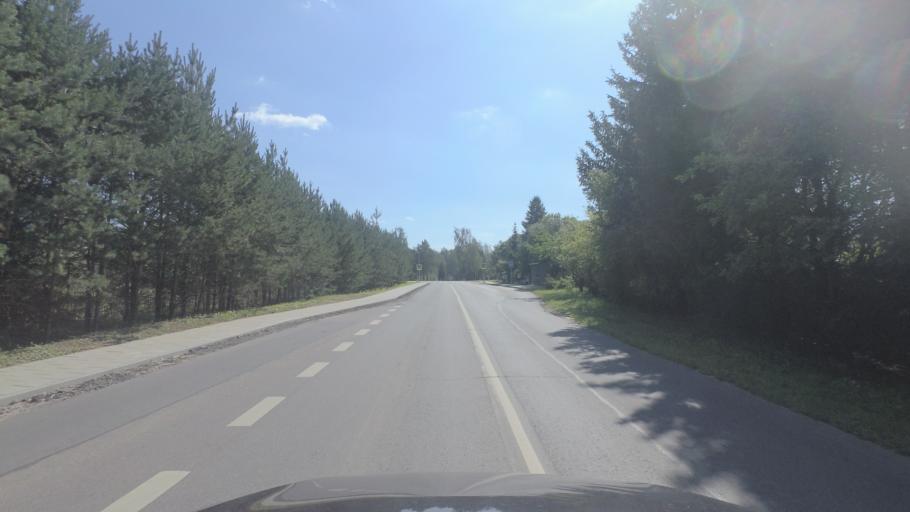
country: LT
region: Vilnius County
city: Rasos
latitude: 54.7921
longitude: 25.3512
